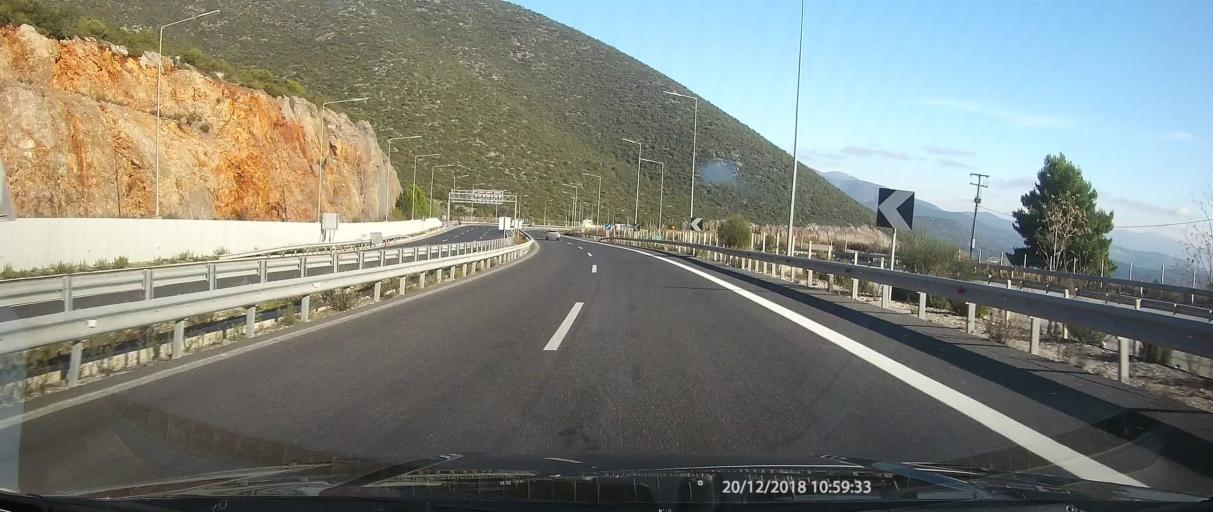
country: GR
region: Peloponnese
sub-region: Nomos Korinthias
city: Nemea
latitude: 37.6994
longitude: 22.5338
